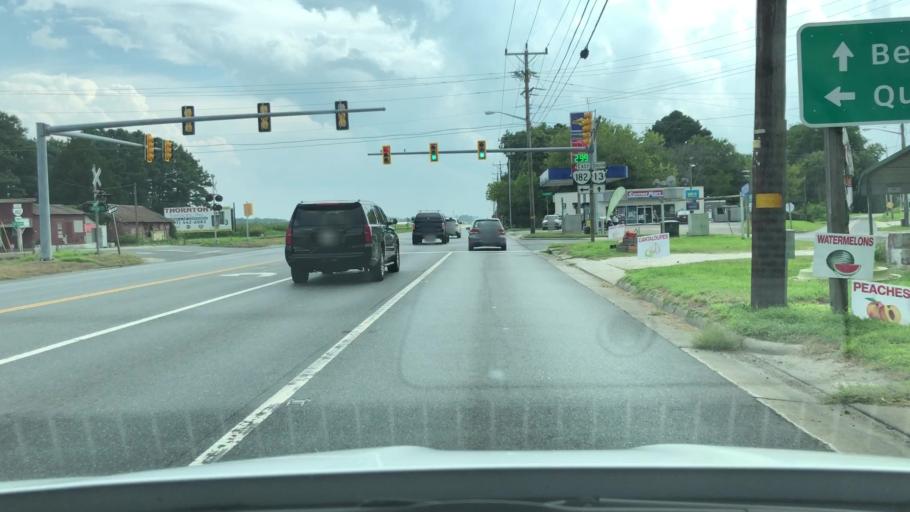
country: US
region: Virginia
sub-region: Northampton County
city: Exmore
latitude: 37.5860
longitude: -75.7850
